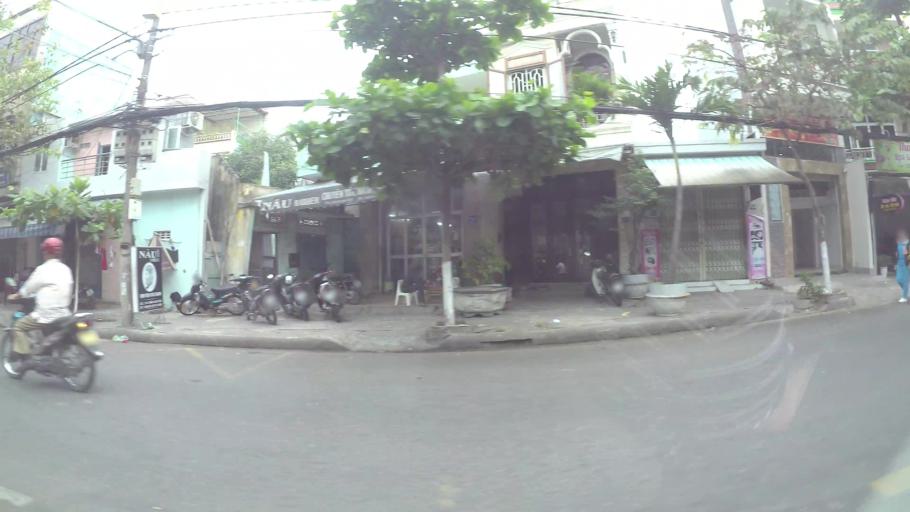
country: VN
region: Da Nang
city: Thanh Khe
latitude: 16.0715
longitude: 108.1876
